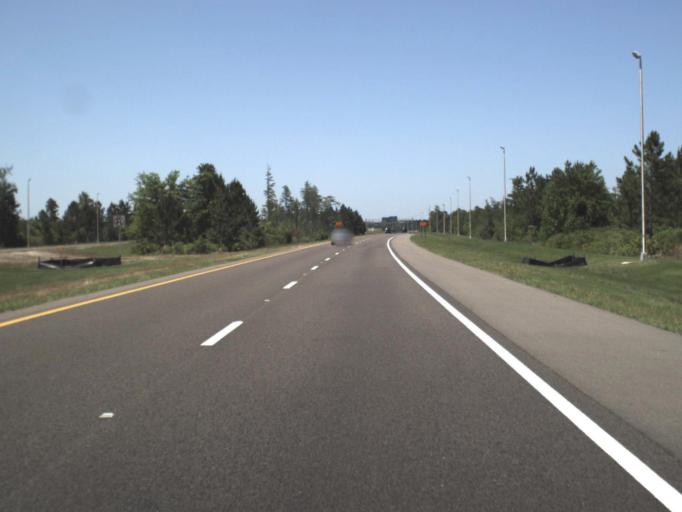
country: US
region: Florida
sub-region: Duval County
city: Baldwin
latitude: 30.2878
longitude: -81.8786
